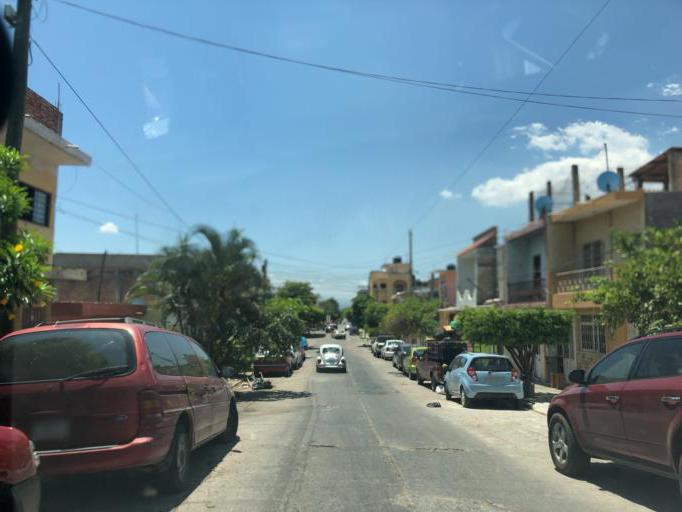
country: MX
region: Chiapas
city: Tuxtla Gutierrez
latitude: 16.7442
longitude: -93.1257
